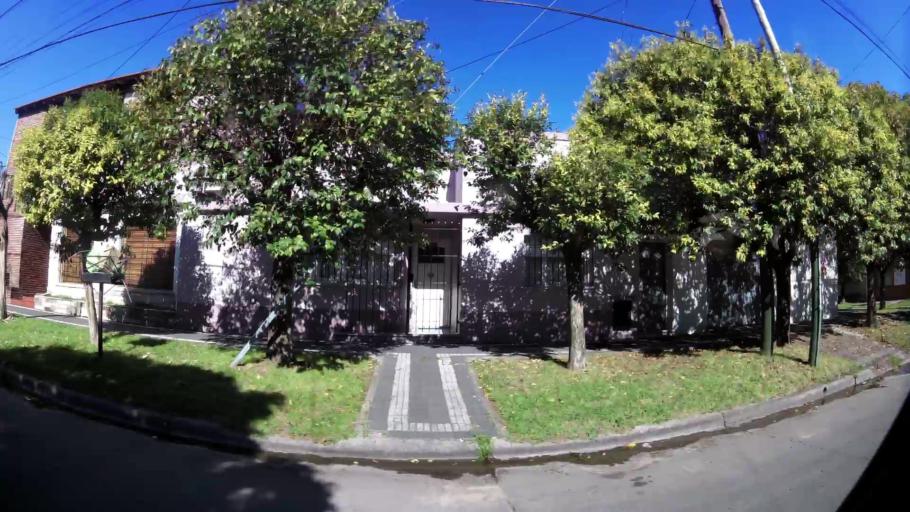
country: AR
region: Buenos Aires
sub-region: Partido de Lomas de Zamora
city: Lomas de Zamora
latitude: -34.7690
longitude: -58.4181
